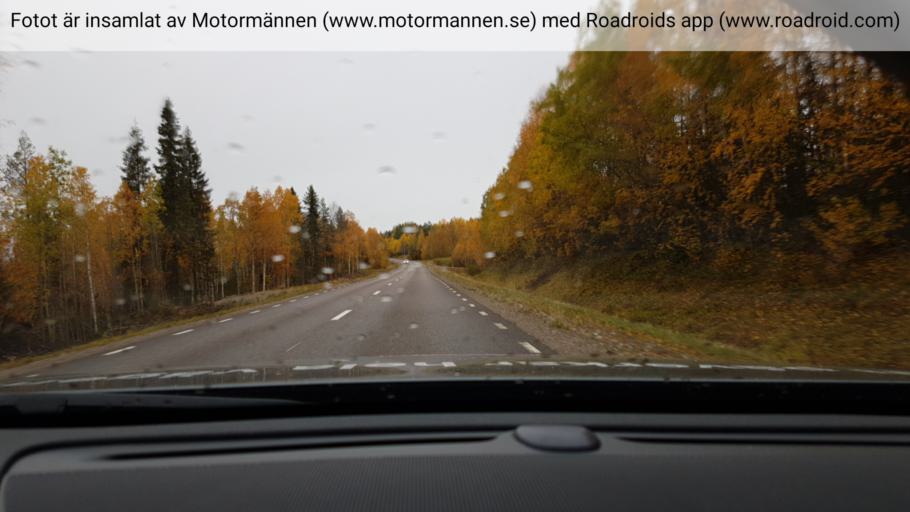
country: SE
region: Norrbotten
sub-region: Overkalix Kommun
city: OEverkalix
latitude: 66.5960
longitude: 22.7596
